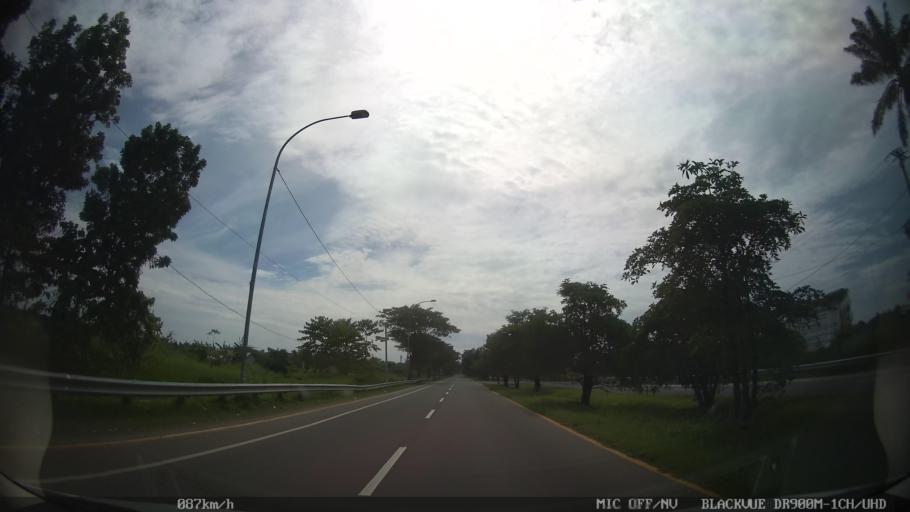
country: ID
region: North Sumatra
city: Percut
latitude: 3.5992
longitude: 98.8247
